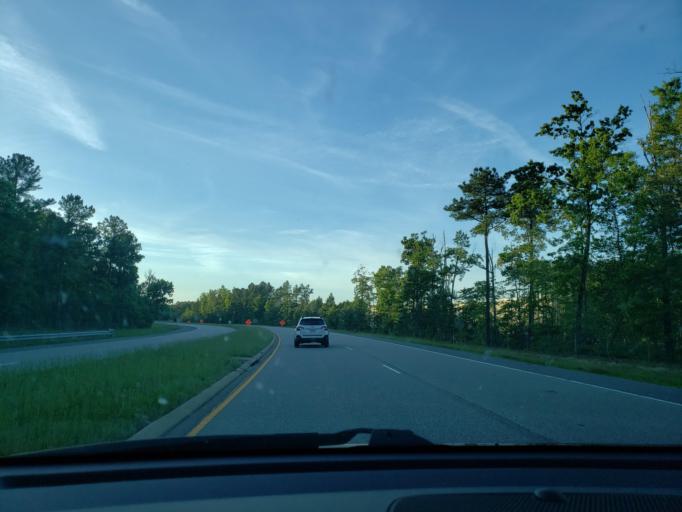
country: US
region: Virginia
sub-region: Henrico County
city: Fort Lee
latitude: 37.4818
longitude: -77.3401
